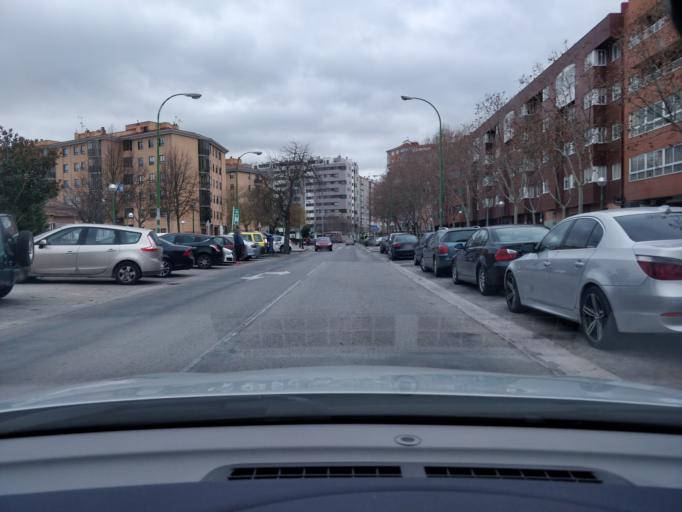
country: ES
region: Castille and Leon
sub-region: Provincia de Burgos
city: Burgos
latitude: 42.3577
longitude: -3.6626
